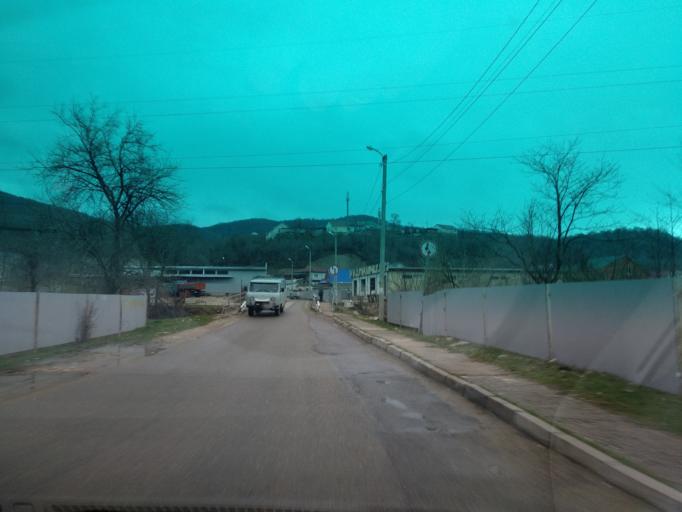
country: RU
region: Krasnodarskiy
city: Novomikhaylovskiy
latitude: 44.2599
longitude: 38.8616
